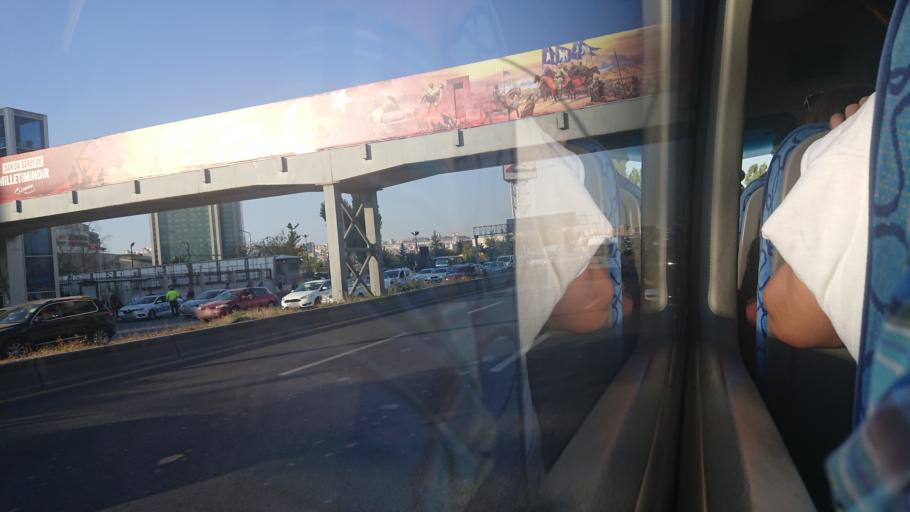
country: TR
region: Ankara
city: Ankara
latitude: 39.9481
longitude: 32.8330
